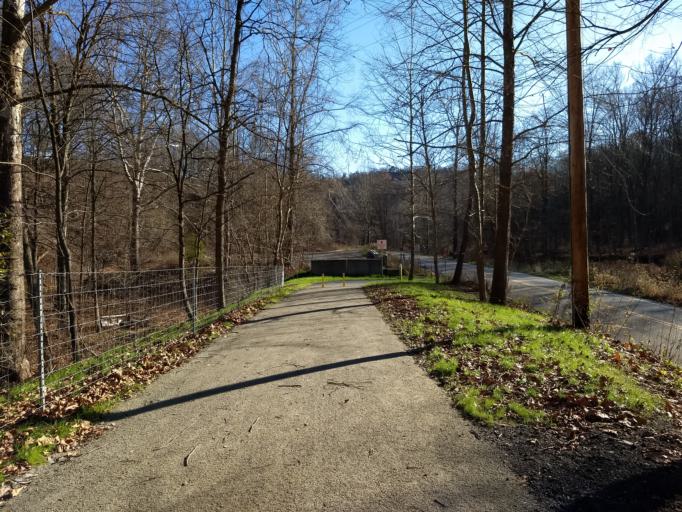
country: US
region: Pennsylvania
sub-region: Washington County
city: Gastonville
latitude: 40.2747
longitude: -79.9708
